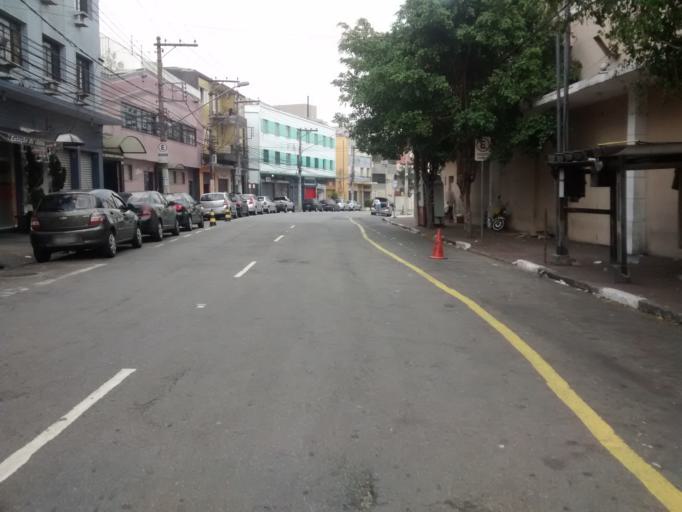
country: BR
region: Sao Paulo
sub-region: Sao Paulo
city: Sao Paulo
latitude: -23.6116
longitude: -46.6363
